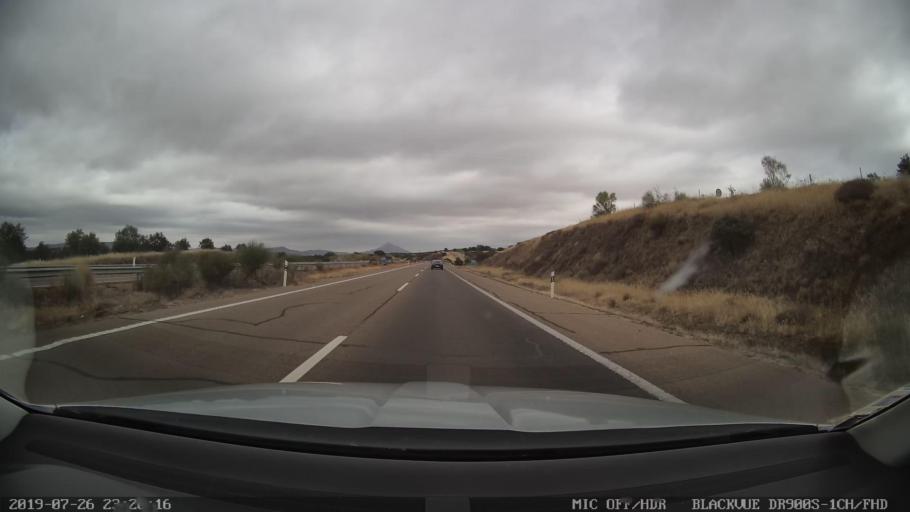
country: ES
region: Extremadura
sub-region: Provincia de Caceres
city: Escurial
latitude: 39.2040
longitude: -5.8791
